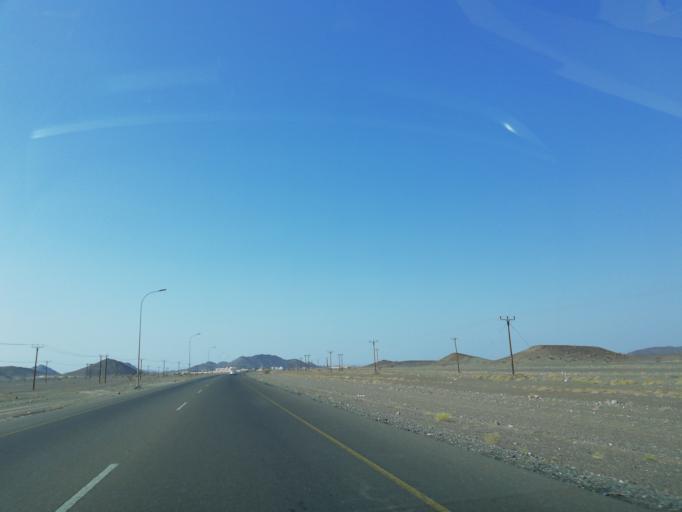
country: OM
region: Ash Sharqiyah
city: Ibra'
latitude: 22.7370
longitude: 58.1504
